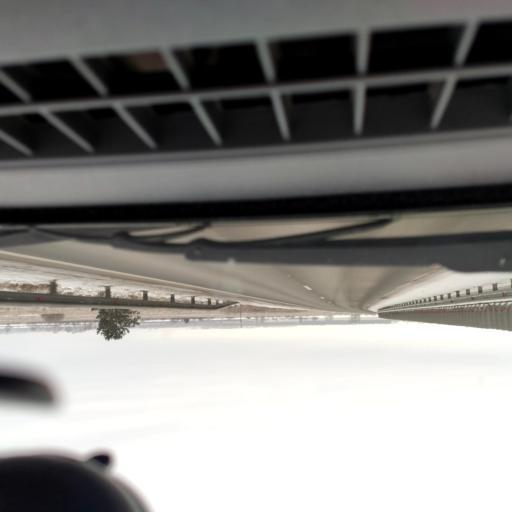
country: RU
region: Bashkortostan
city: Kushnarenkovo
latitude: 55.0669
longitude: 55.3598
